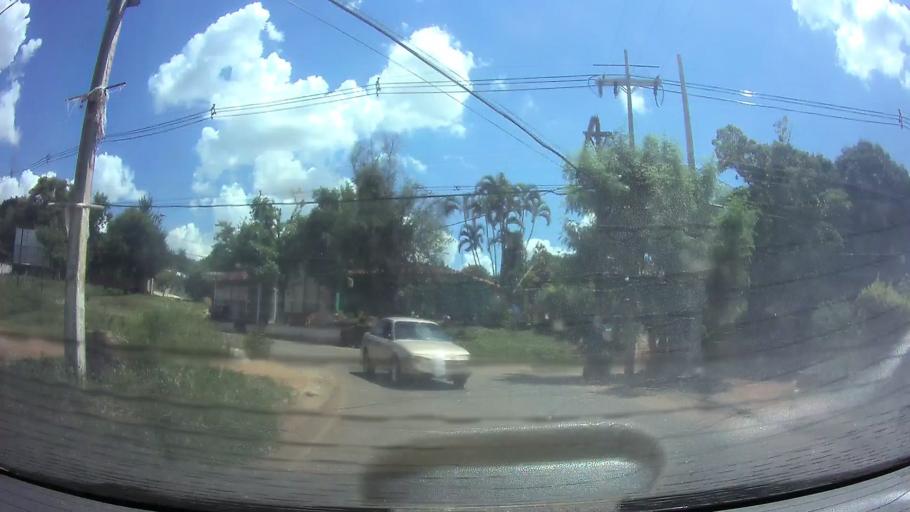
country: PY
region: Central
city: Limpio
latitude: -25.1676
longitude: -57.4449
